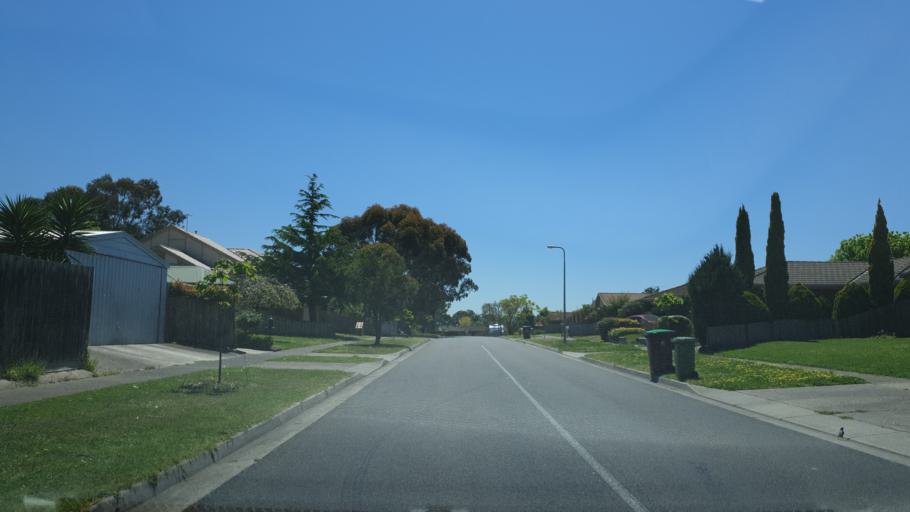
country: AU
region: Victoria
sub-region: Casey
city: Cranbourne North
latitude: -38.0804
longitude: 145.2911
